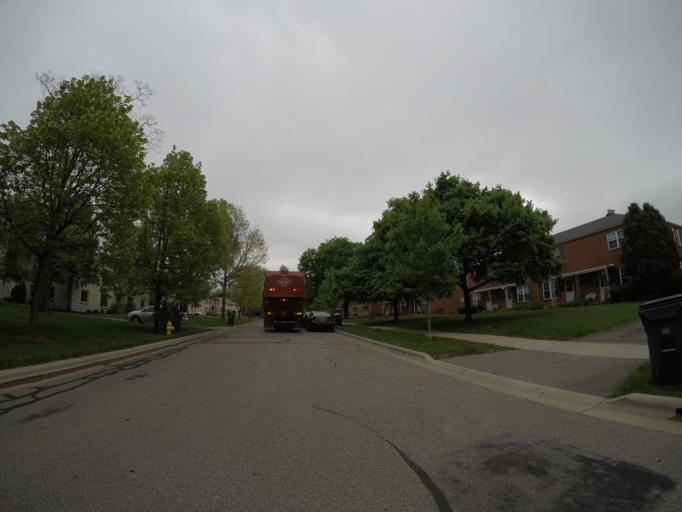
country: US
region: Ohio
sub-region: Franklin County
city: Upper Arlington
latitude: 40.0160
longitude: -83.0680
